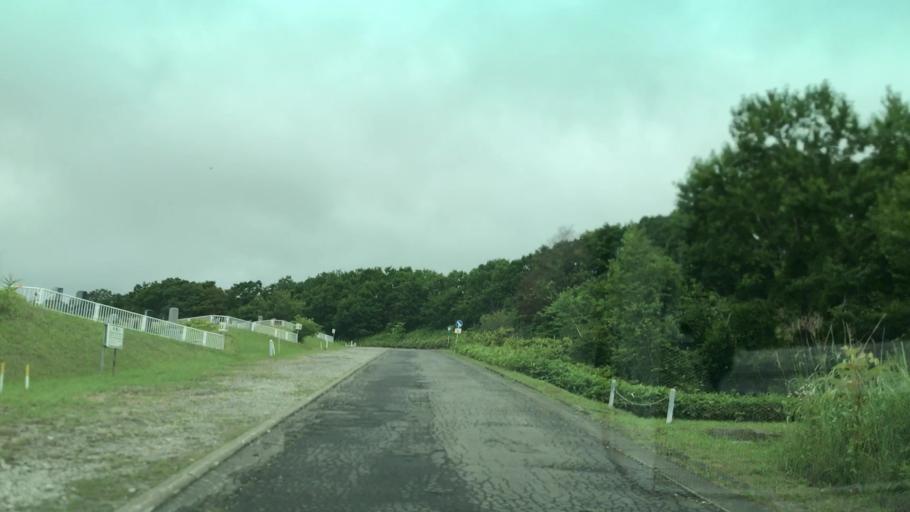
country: JP
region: Hokkaido
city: Muroran
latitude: 42.3957
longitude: 141.0010
